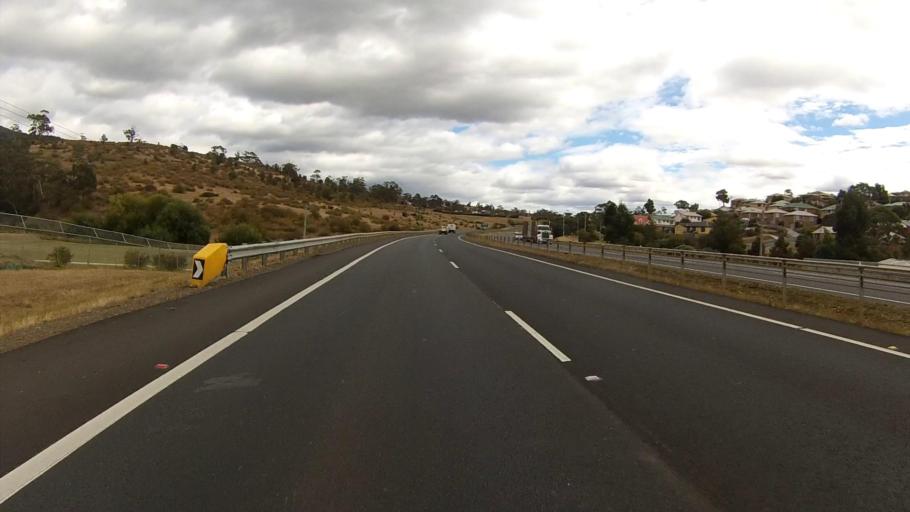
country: AU
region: Tasmania
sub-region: Glenorchy
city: Claremont
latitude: -42.7844
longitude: 147.2410
